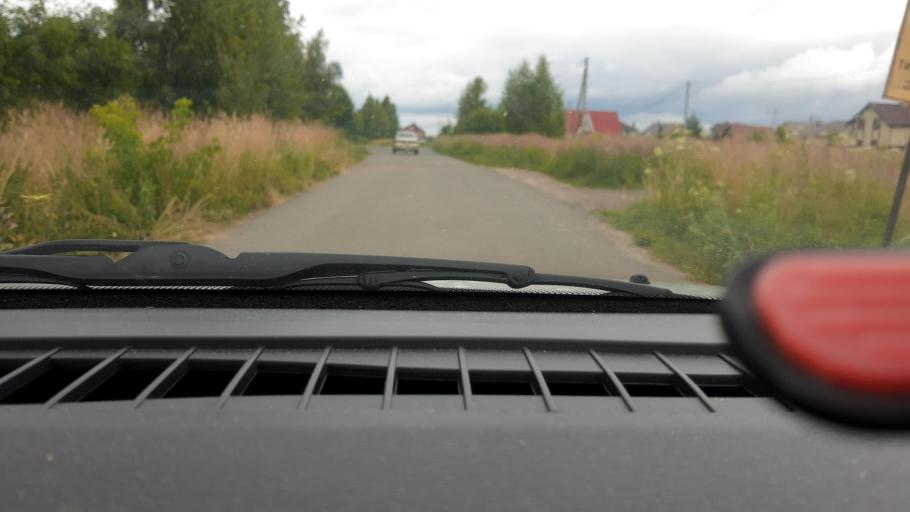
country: RU
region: Nizjnij Novgorod
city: Nizhniy Novgorod
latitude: 56.2160
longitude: 43.9597
